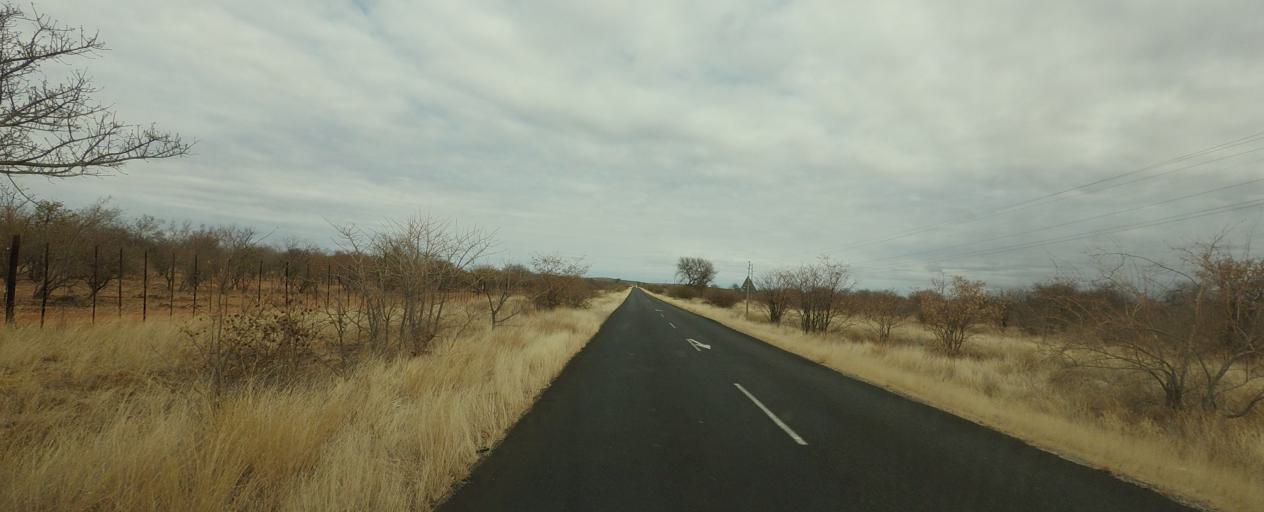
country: ZW
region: Matabeleland South
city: Beitbridge
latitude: -22.4315
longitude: 29.4653
